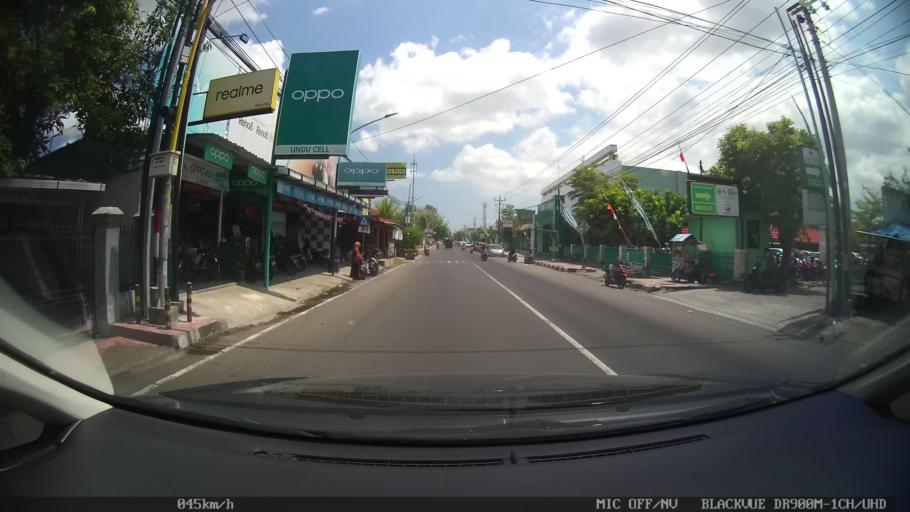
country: ID
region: Daerah Istimewa Yogyakarta
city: Bantul
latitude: -7.8934
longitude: 110.3395
